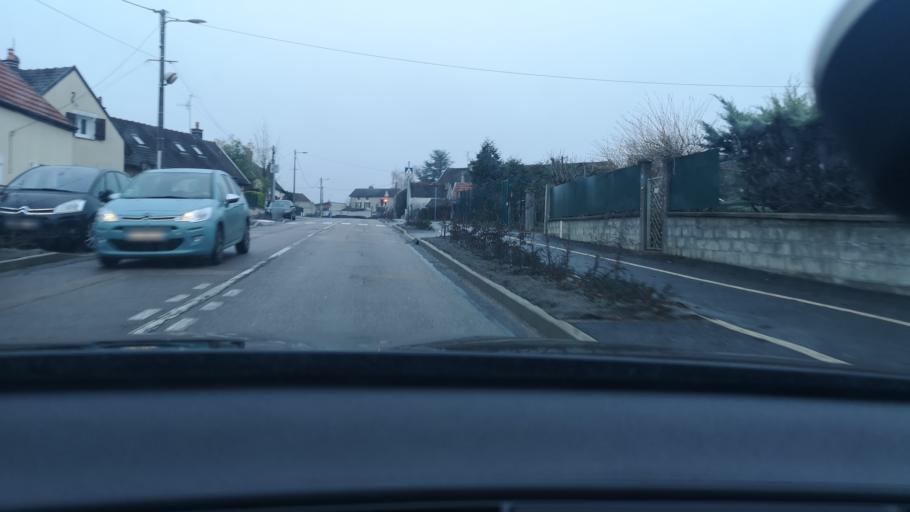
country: FR
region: Bourgogne
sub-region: Departement de la Cote-d'Or
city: Fenay
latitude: 47.2214
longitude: 5.0639
